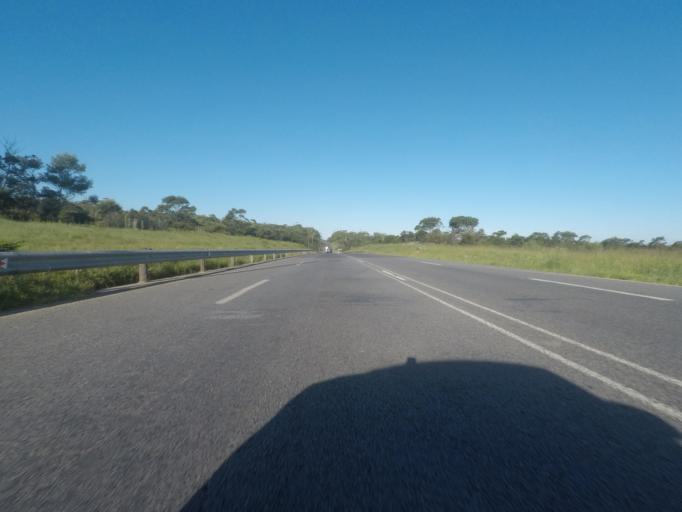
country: ZA
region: Eastern Cape
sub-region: Buffalo City Metropolitan Municipality
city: East London
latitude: -33.0486
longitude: 27.8184
